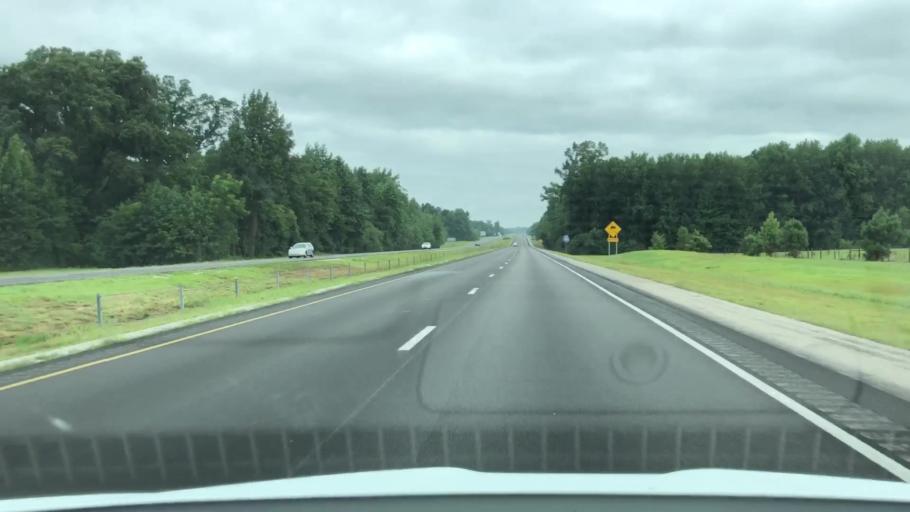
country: US
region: North Carolina
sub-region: Wayne County
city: Fremont
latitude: 35.5557
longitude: -77.9869
